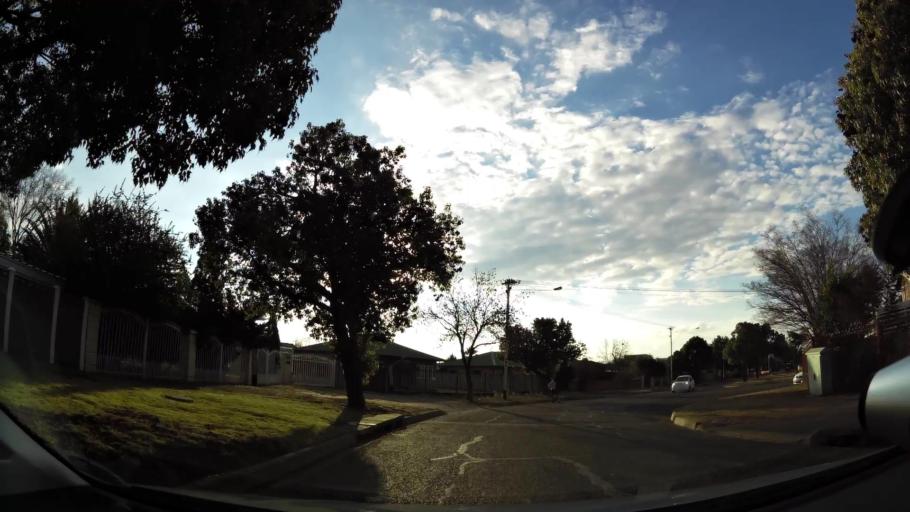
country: ZA
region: Orange Free State
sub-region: Mangaung Metropolitan Municipality
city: Bloemfontein
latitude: -29.1373
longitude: 26.1961
